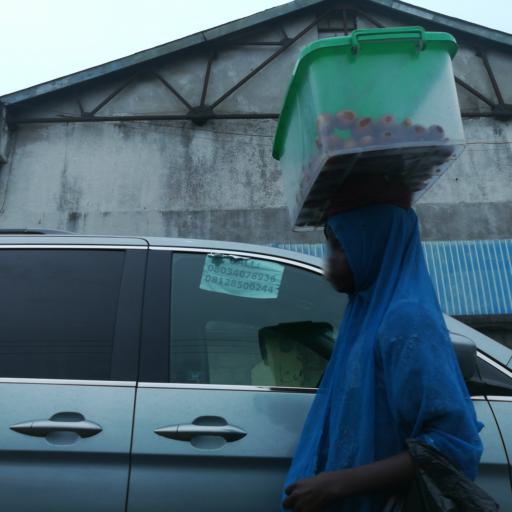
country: NG
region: Lagos
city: Ebute Metta
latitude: 6.4787
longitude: 3.3845
